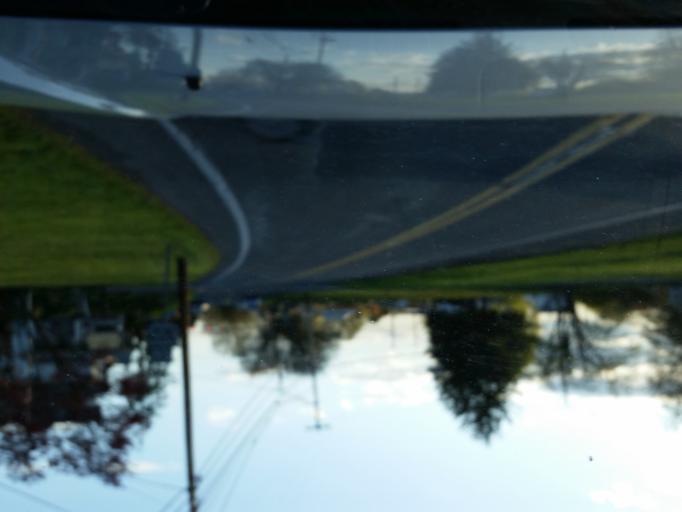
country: US
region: Pennsylvania
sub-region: Dauphin County
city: Hershey
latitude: 40.2717
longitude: -76.6552
